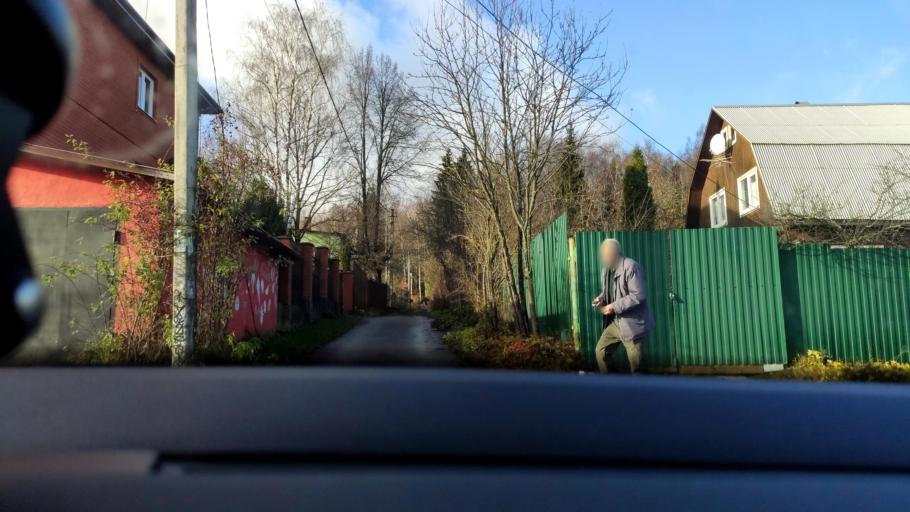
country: RU
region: Moskovskaya
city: Yermolino
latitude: 56.1596
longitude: 37.4766
